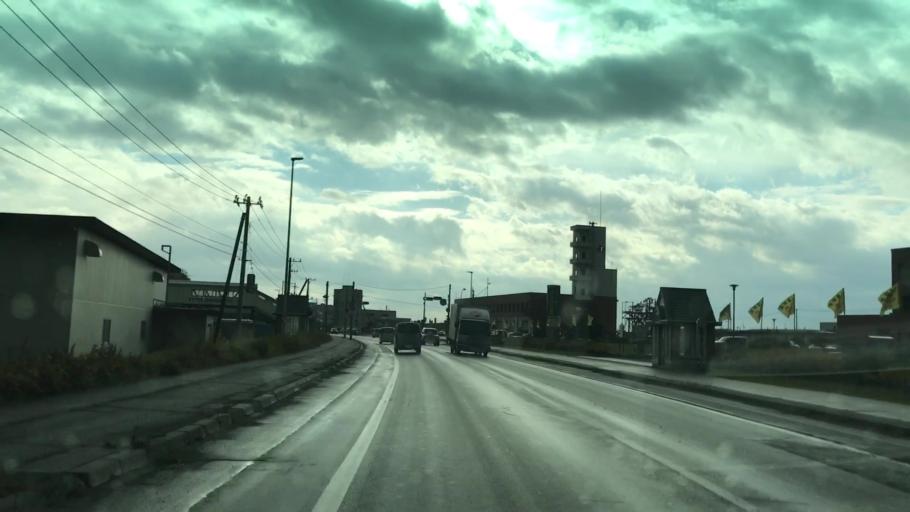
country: JP
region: Hokkaido
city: Shizunai-furukawacho
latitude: 42.1693
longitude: 142.7687
